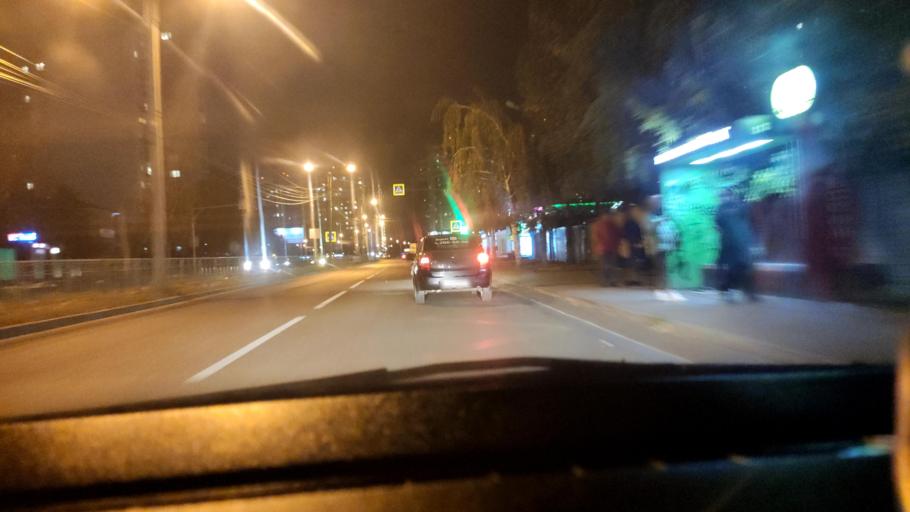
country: RU
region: Voronezj
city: Voronezh
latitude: 51.7104
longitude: 39.1952
